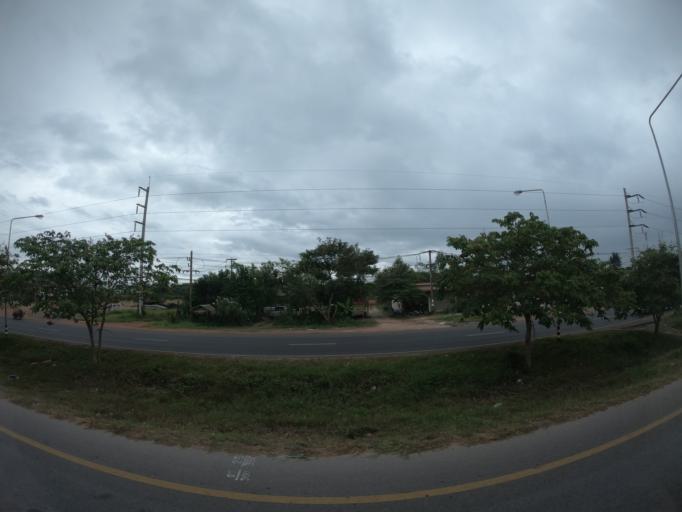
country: TH
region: Roi Et
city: Roi Et
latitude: 16.0521
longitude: 103.6204
